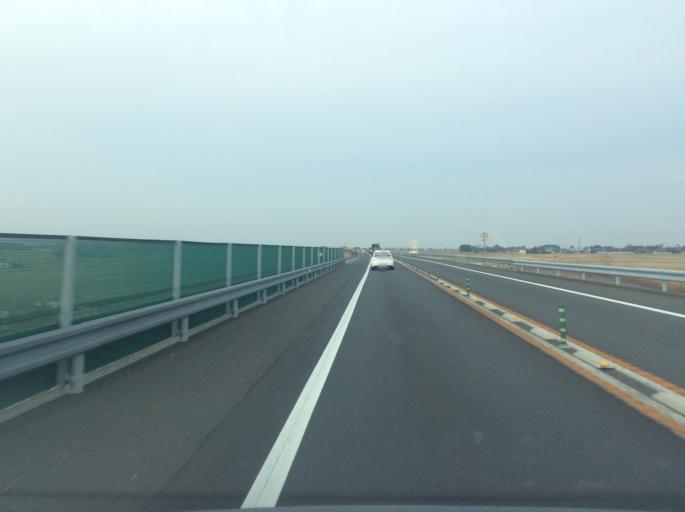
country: JP
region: Miyagi
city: Watari
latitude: 38.0559
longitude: 140.8938
